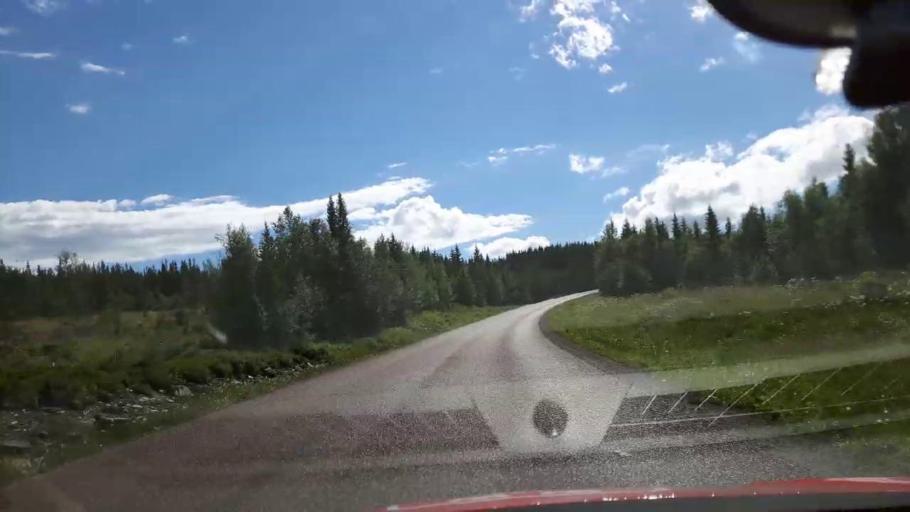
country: SE
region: Jaemtland
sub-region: Are Kommun
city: Are
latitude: 63.2800
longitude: 13.2365
